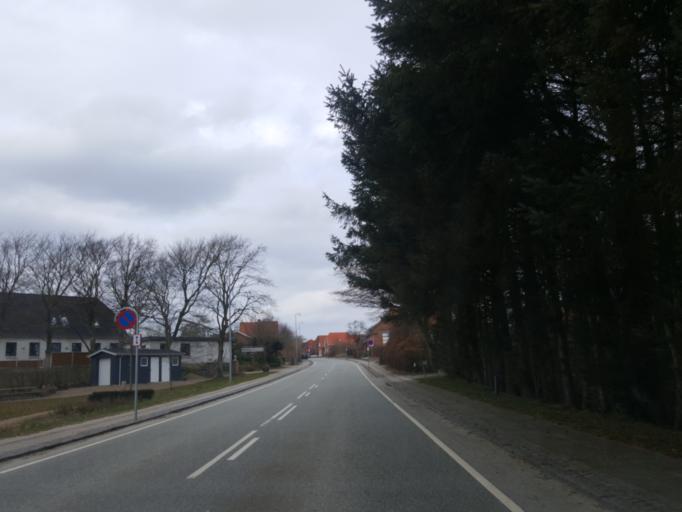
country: DK
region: Central Jutland
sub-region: Lemvig Kommune
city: Lemvig
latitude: 56.4323
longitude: 8.2088
